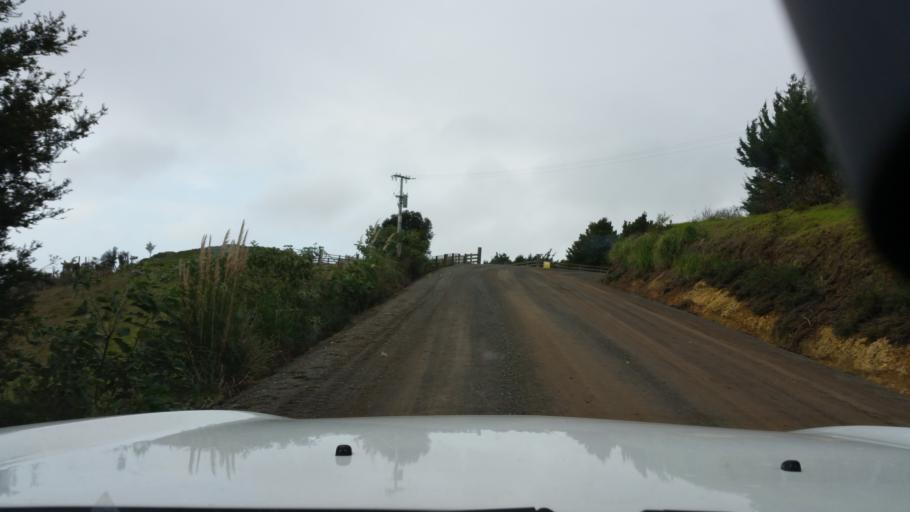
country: NZ
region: Northland
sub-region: Whangarei
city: Ngunguru
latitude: -35.7400
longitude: 174.4917
